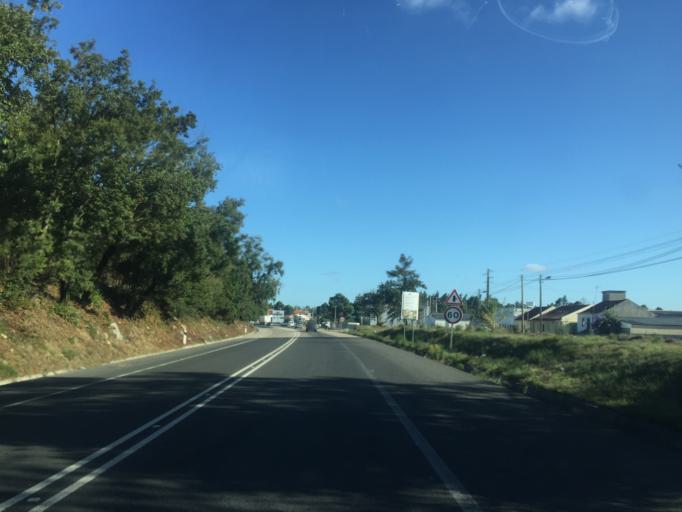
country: PT
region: Leiria
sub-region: Porto de Mos
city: Porto de Mos
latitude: 39.5955
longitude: -8.8594
